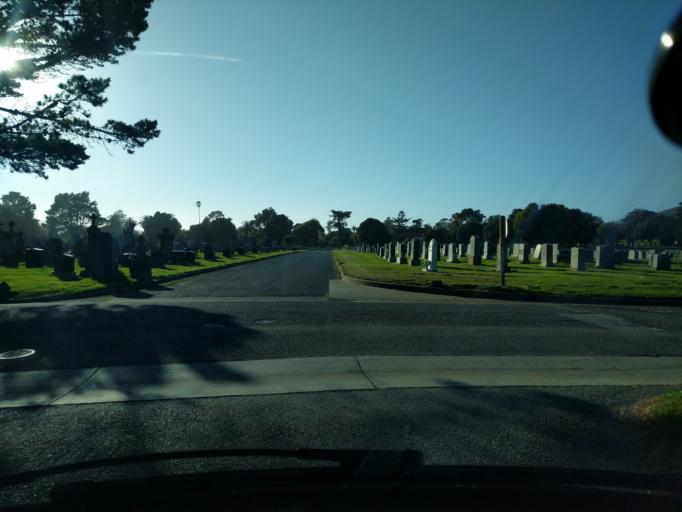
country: US
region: California
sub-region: San Mateo County
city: Colma
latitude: 37.6733
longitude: -122.4475
